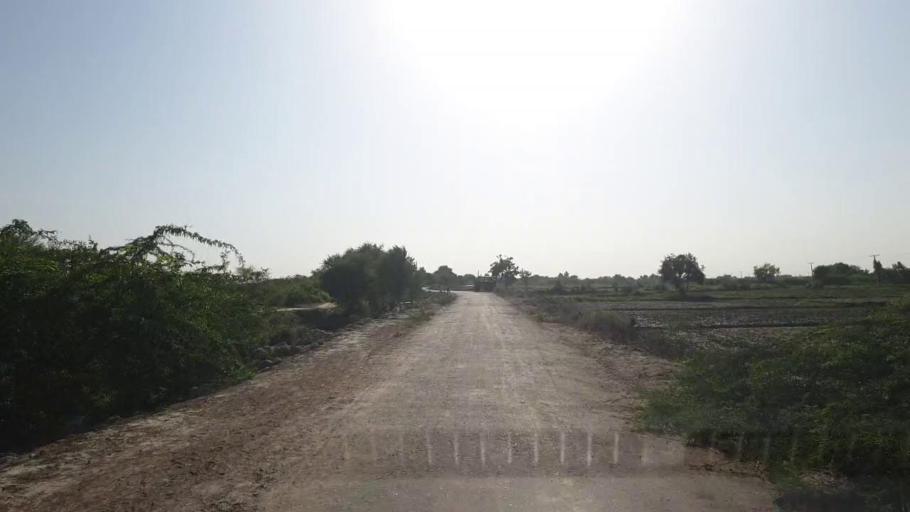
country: PK
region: Sindh
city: Badin
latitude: 24.6009
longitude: 68.9151
